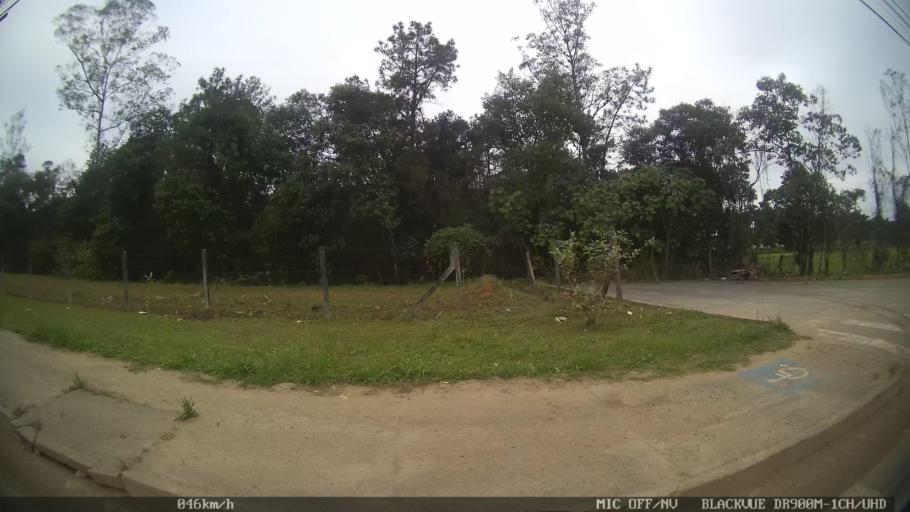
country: BR
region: Santa Catarina
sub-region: Joinville
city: Joinville
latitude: -26.3375
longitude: -48.8954
